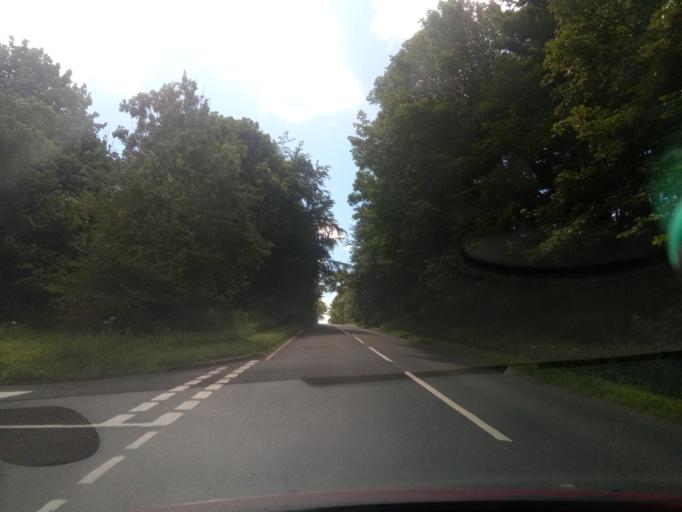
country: GB
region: England
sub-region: Northumberland
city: Acomb
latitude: 55.0746
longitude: -2.0910
